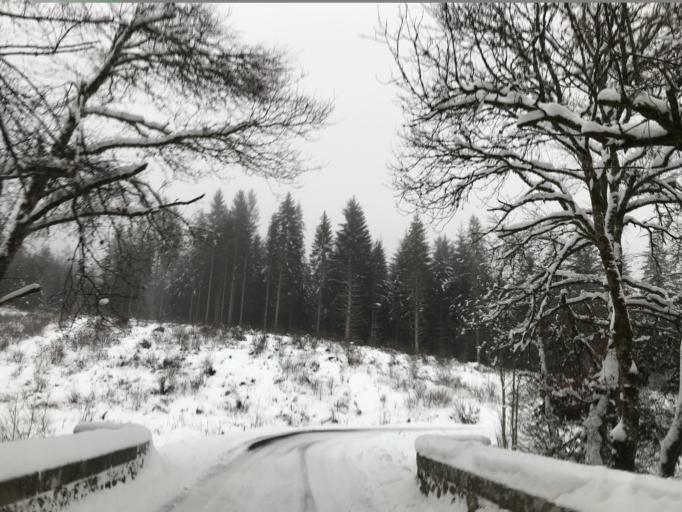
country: FR
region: Rhone-Alpes
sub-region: Departement de la Loire
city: Noiretable
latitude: 45.7228
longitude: 3.6991
